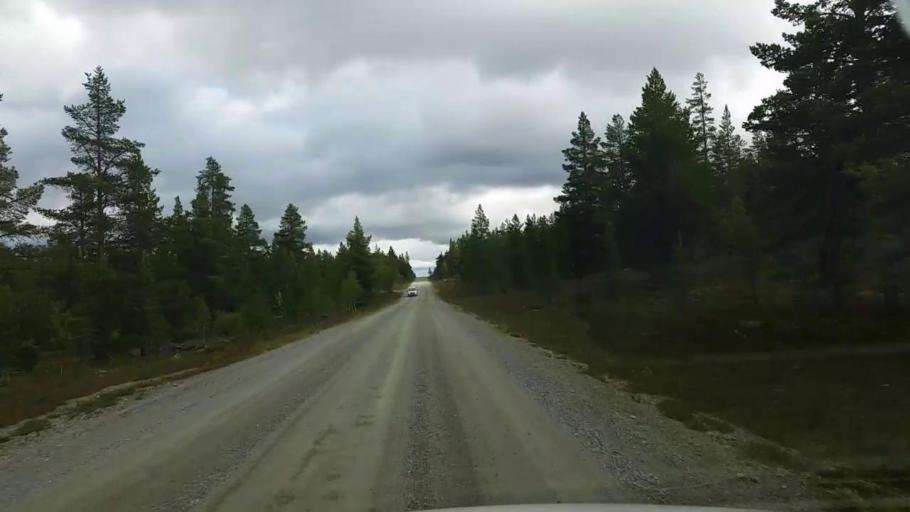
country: NO
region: Hedmark
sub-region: Engerdal
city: Engerdal
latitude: 62.3369
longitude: 12.6248
